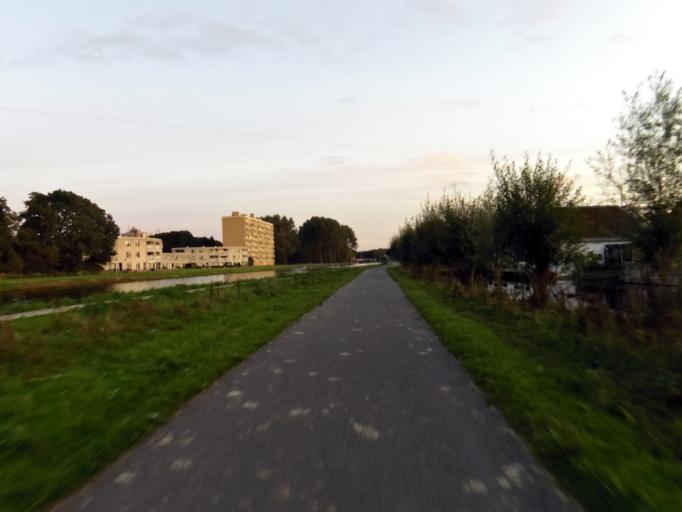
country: NL
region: South Holland
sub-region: Gemeente Voorschoten
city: Voorschoten
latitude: 52.1419
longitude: 4.4661
